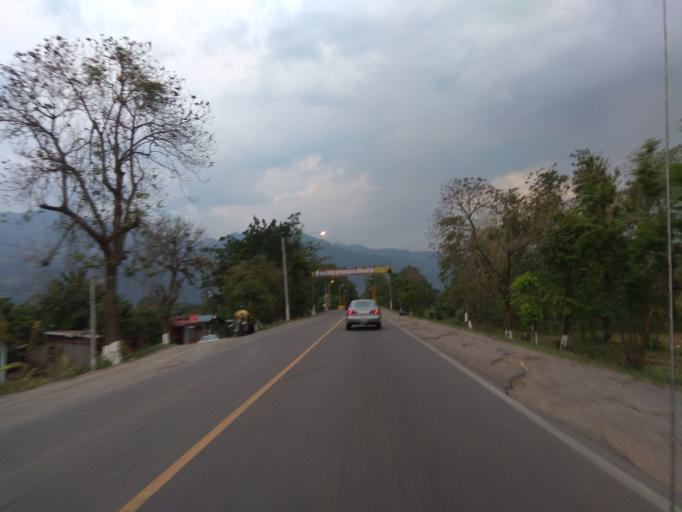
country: HN
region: Yoro
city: El Progreso
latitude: 15.3754
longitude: -87.8032
